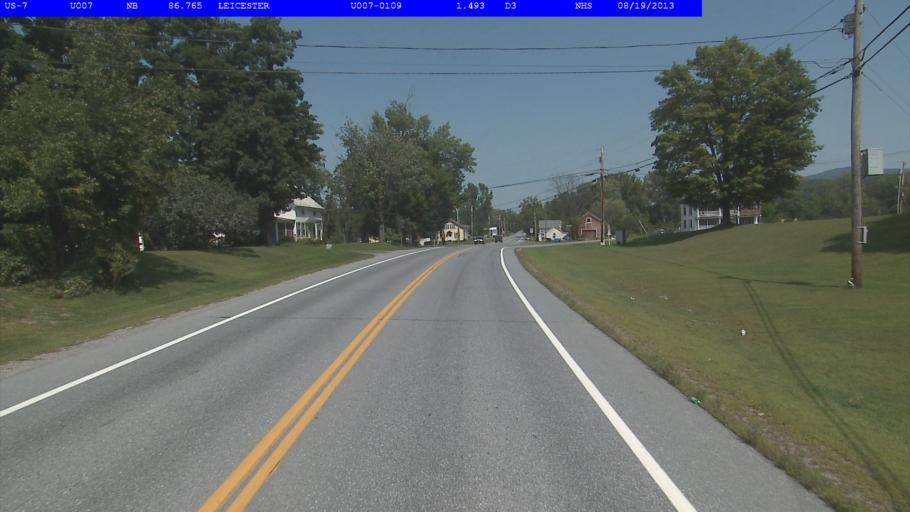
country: US
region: Vermont
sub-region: Rutland County
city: Brandon
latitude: 43.8649
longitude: -73.1075
